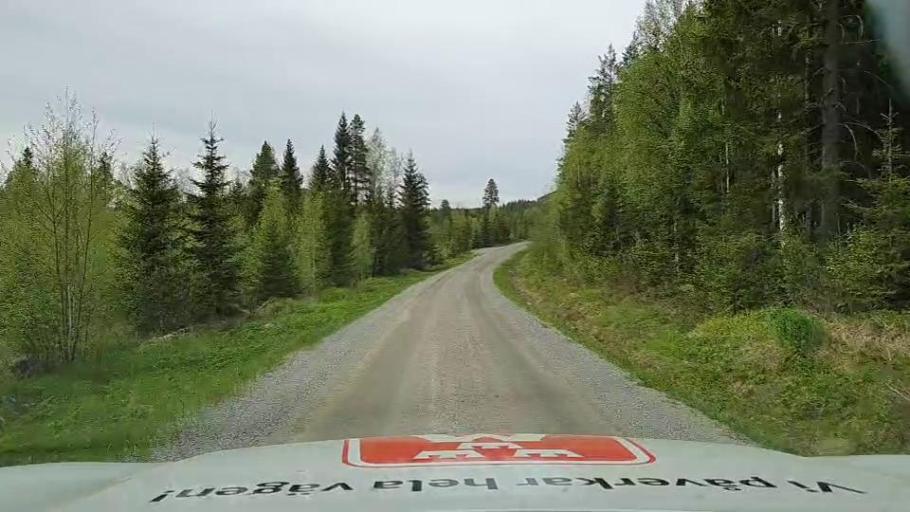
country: SE
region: Jaemtland
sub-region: Bergs Kommun
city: Hoverberg
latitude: 62.5209
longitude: 14.9134
